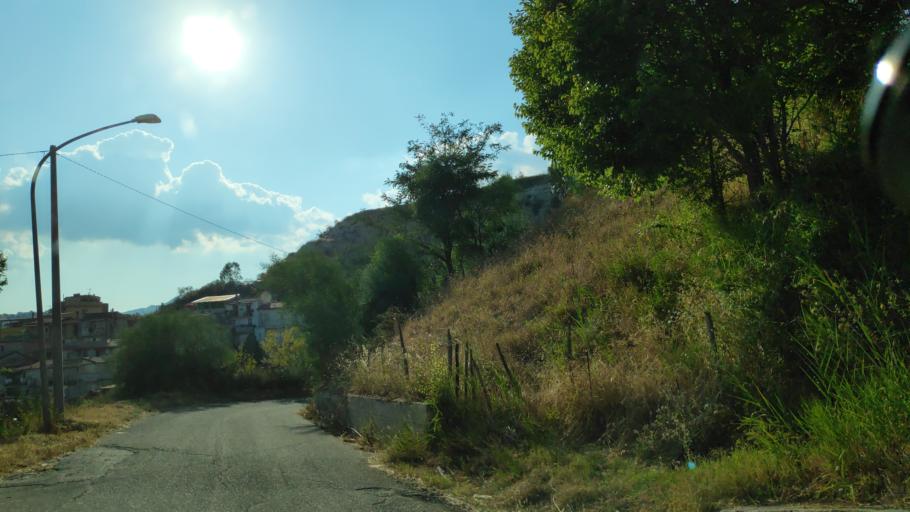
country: IT
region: Calabria
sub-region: Provincia di Catanzaro
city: Guardavalle
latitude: 38.5070
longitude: 16.5078
